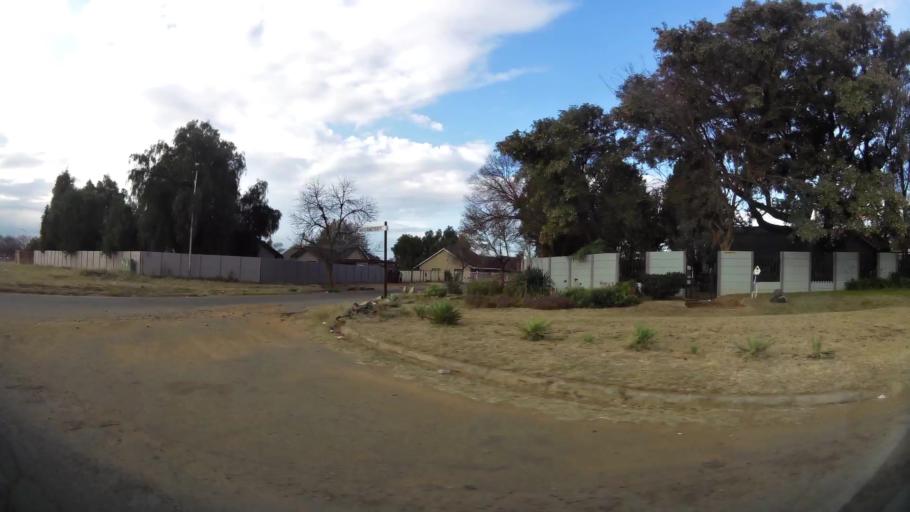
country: ZA
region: Orange Free State
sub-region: Lejweleputswa District Municipality
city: Welkom
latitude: -28.0000
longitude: 26.7349
